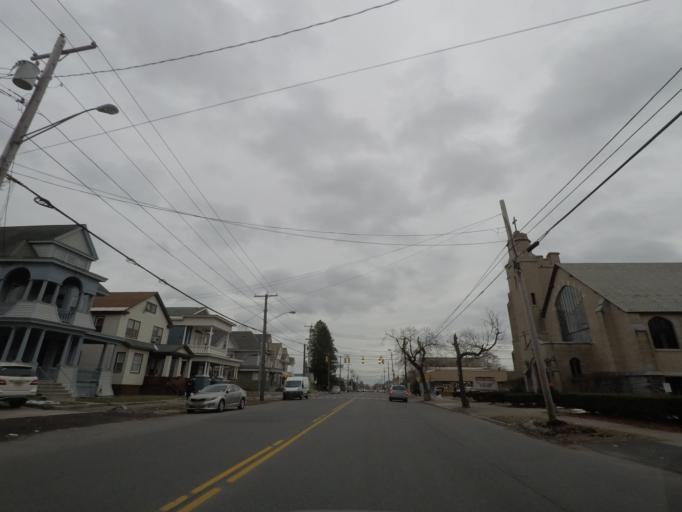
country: US
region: New York
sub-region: Schenectady County
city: Schenectady
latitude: 42.8035
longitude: -73.9303
